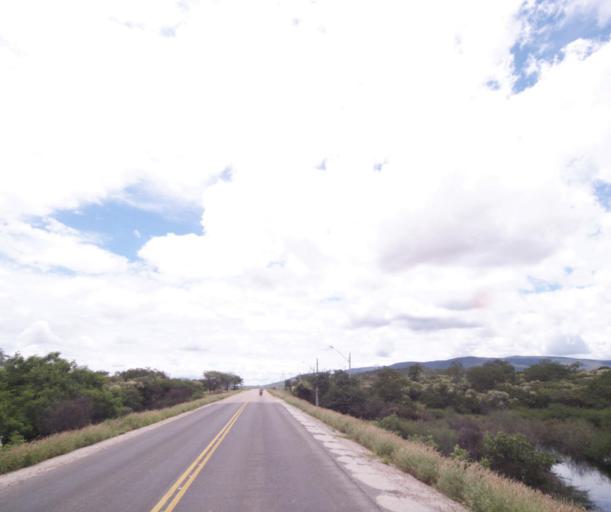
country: BR
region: Bahia
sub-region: Brumado
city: Brumado
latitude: -14.2141
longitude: -41.6433
